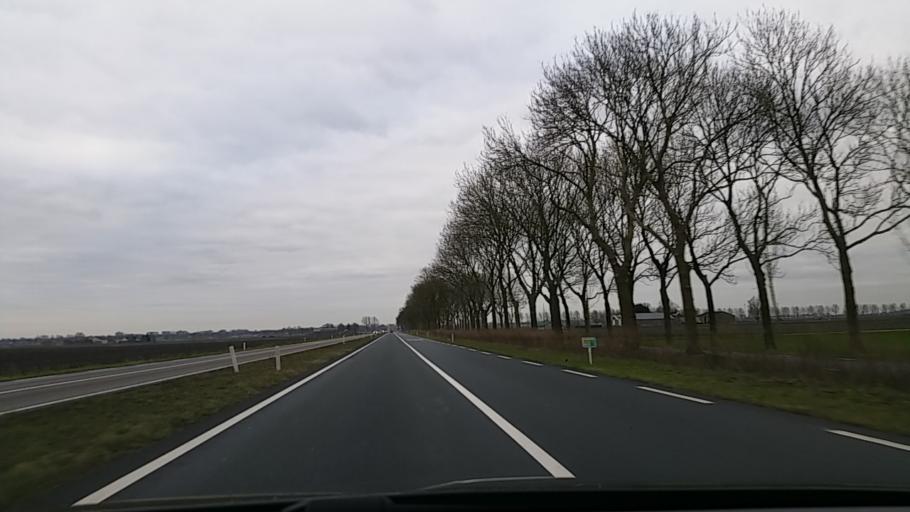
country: NL
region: South Holland
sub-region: Gemeente Kaag en Braassem
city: Oude Wetering
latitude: 52.1775
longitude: 4.6706
